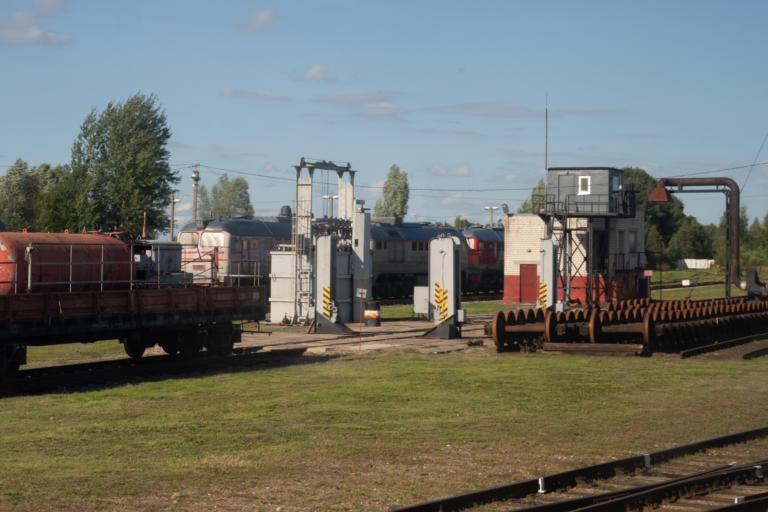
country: RU
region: Kaliningrad
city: Chernyakhovsk
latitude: 54.6019
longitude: 21.7478
